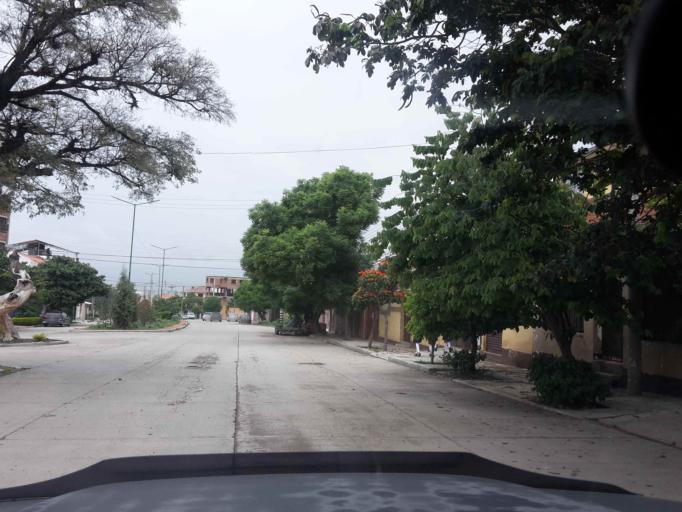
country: BO
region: Cochabamba
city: Cochabamba
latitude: -17.3768
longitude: -66.1204
